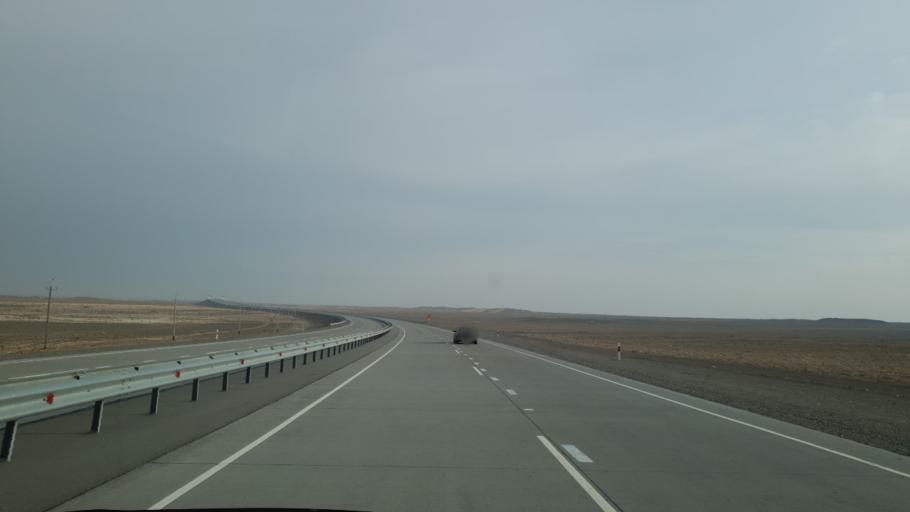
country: KZ
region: Almaty Oblysy
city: Kegen
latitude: 43.7582
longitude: 79.1348
